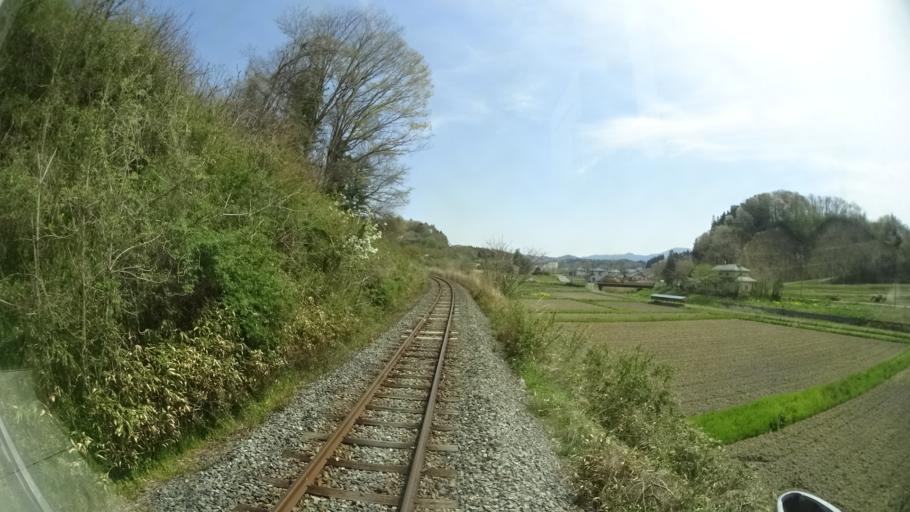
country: JP
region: Iwate
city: Ichinoseki
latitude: 38.9946
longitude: 141.3106
